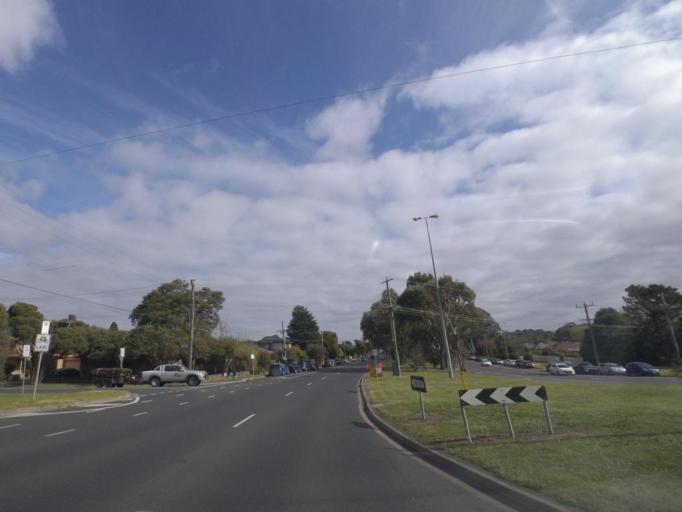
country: AU
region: Victoria
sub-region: Maroondah
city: Ringwood East
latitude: -37.8082
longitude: 145.2517
